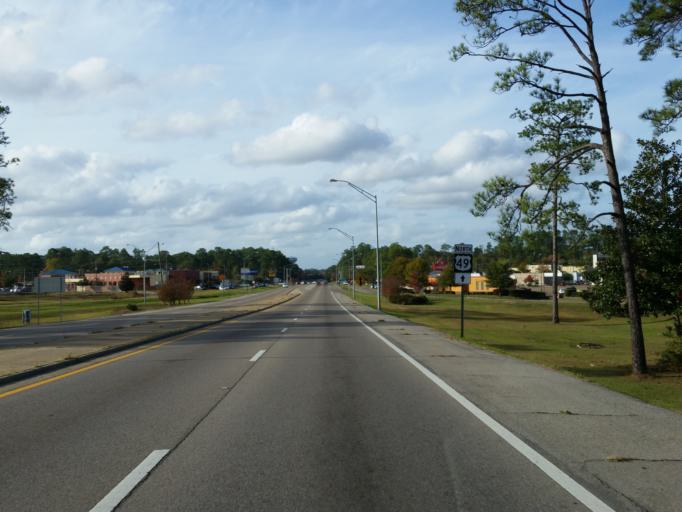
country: US
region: Mississippi
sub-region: Forrest County
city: Hattiesburg
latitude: 31.3082
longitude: -89.3174
